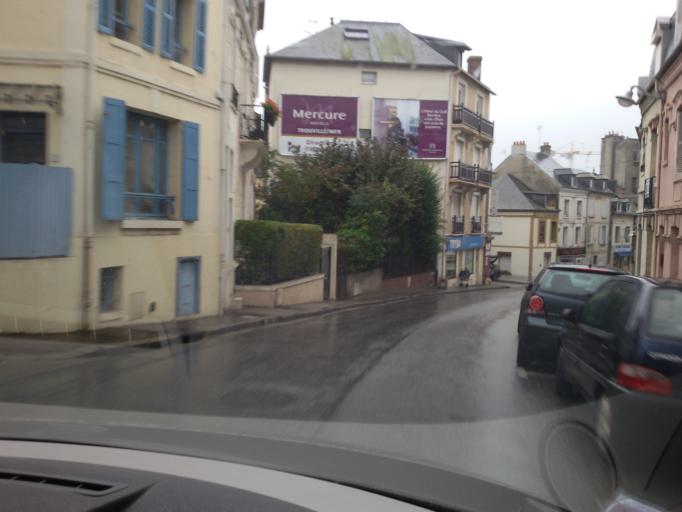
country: FR
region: Lower Normandy
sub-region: Departement du Calvados
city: Trouville-sur-Mer
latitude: 49.3625
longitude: 0.0863
